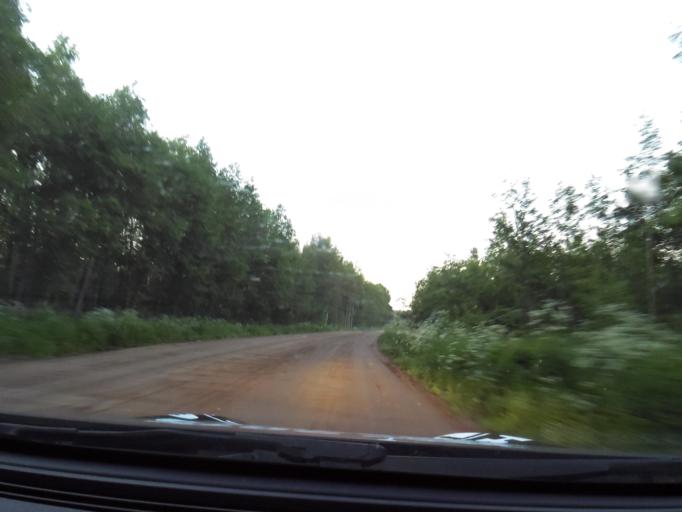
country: RU
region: Leningrad
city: Voznesen'ye
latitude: 60.8562
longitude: 35.9273
